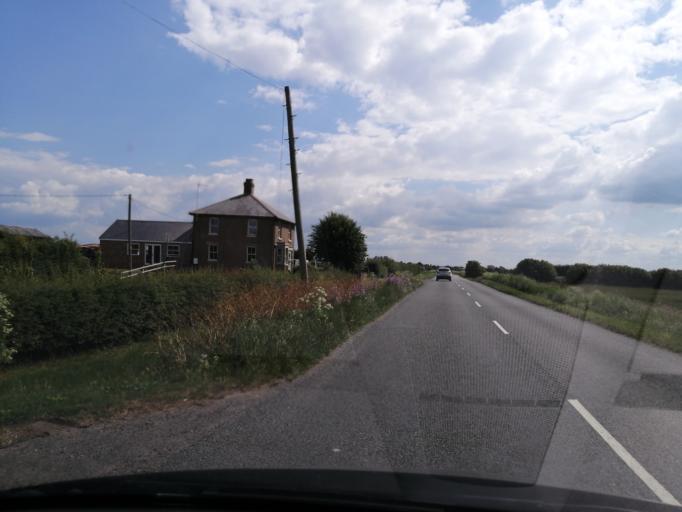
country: GB
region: England
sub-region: Cambridgeshire
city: Ramsey
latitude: 52.4633
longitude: -0.1548
